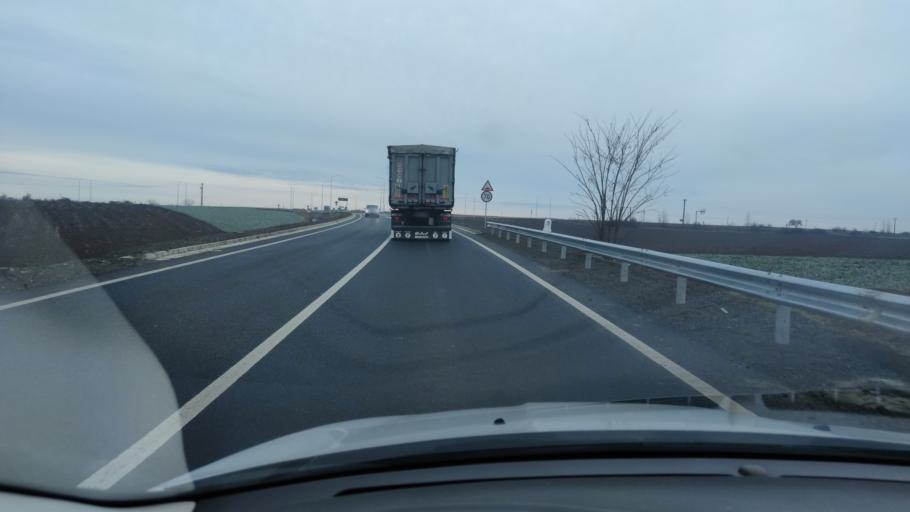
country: RO
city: Szekelyhid
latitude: 47.3504
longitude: 22.1279
